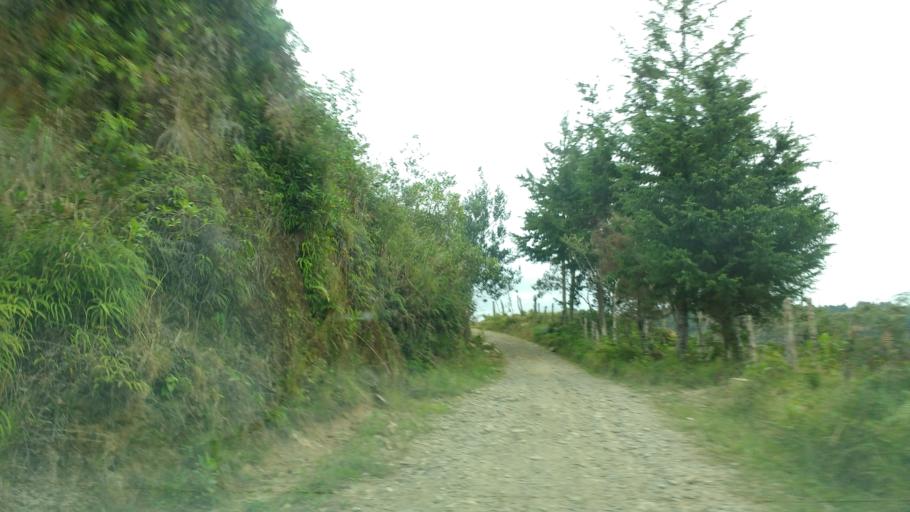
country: CO
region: Antioquia
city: Concepcion
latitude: 6.3670
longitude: -75.2286
